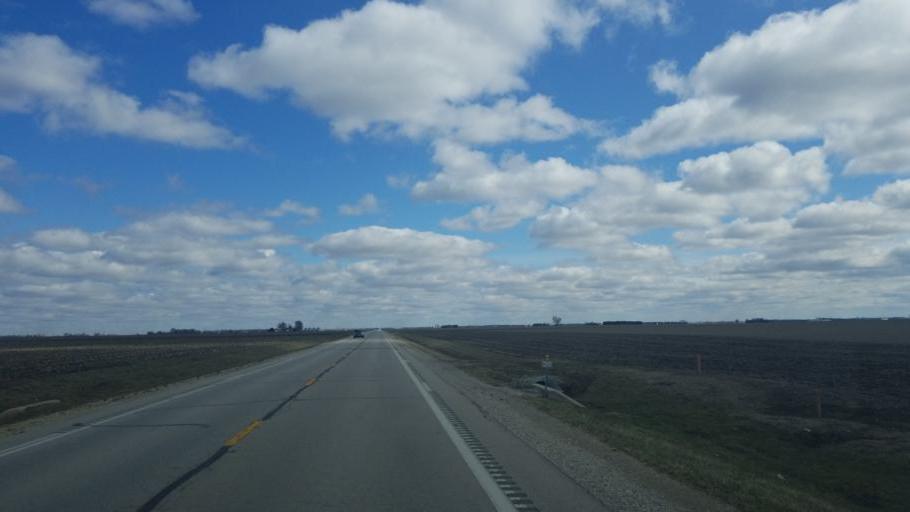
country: US
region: Illinois
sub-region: Douglas County
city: Villa Grove
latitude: 39.7920
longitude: -88.1394
